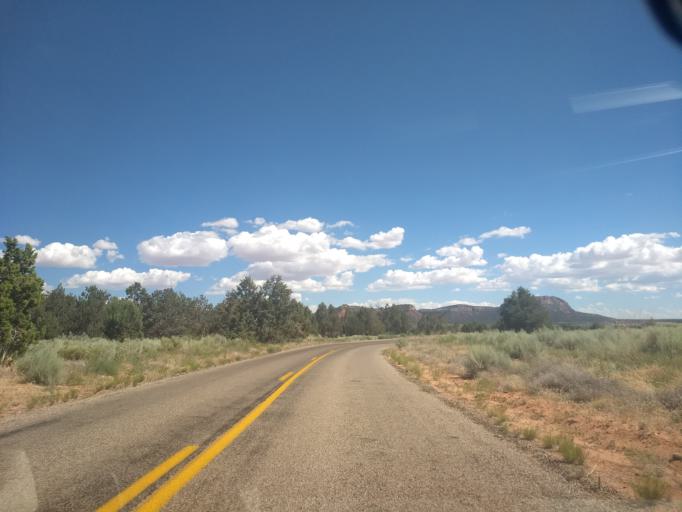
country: US
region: Utah
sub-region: Washington County
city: Hildale
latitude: 36.9662
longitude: -112.8706
